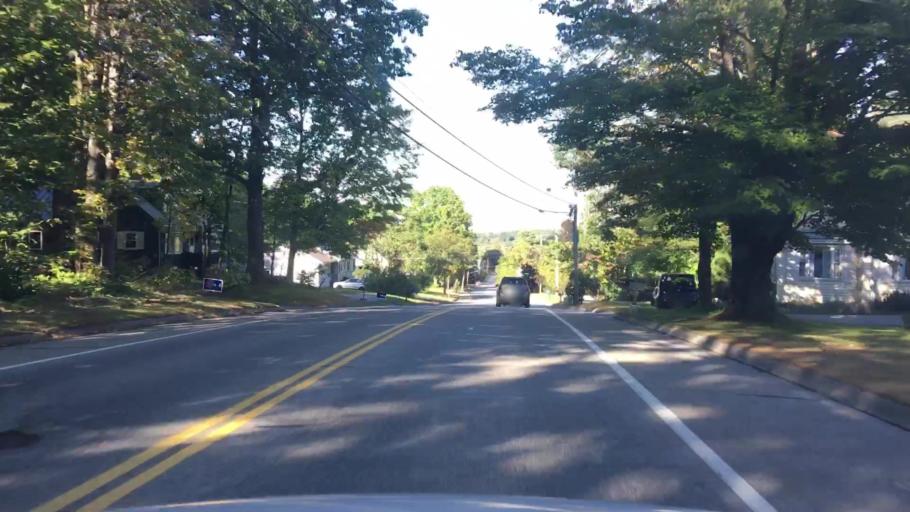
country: US
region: Maine
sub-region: Androscoggin County
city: Lewiston
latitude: 44.0880
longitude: -70.1653
